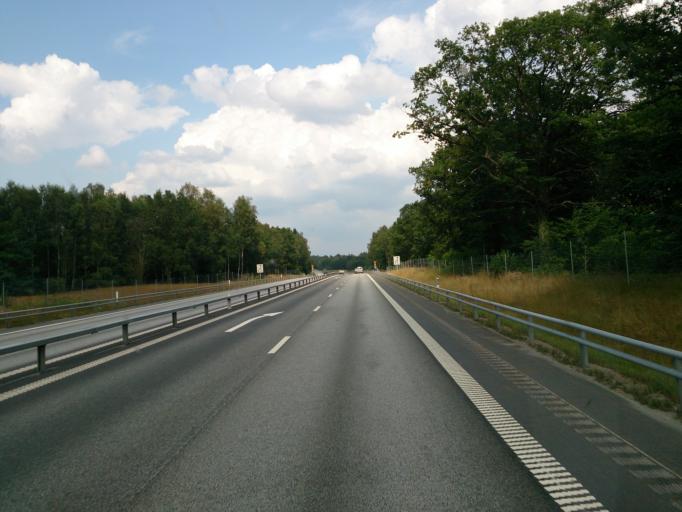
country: SE
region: Skane
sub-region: Horby Kommun
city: Hoerby
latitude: 55.9194
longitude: 13.7838
